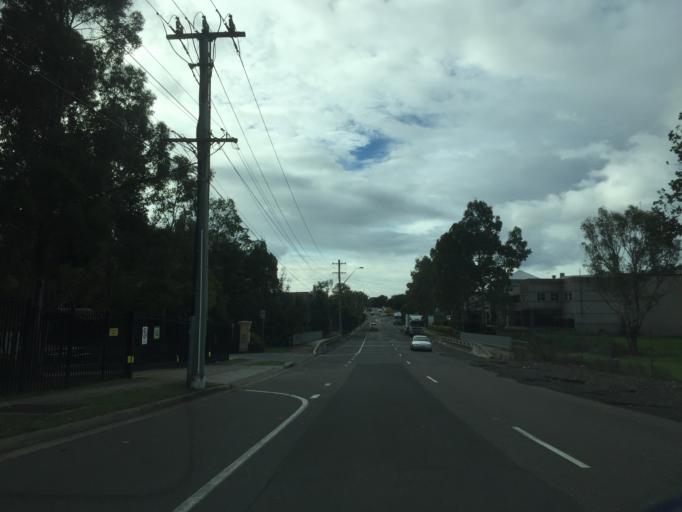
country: AU
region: New South Wales
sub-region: Blacktown
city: Doonside
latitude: -33.7928
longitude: 150.8899
